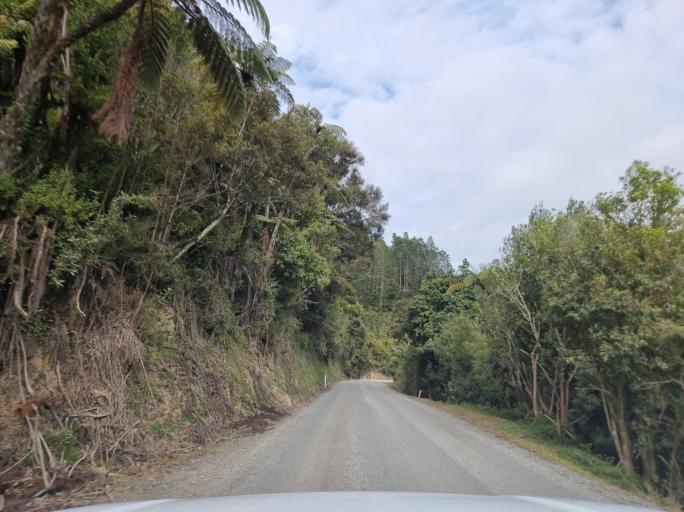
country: NZ
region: Northland
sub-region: Whangarei
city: Ruakaka
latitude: -36.0525
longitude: 174.3992
